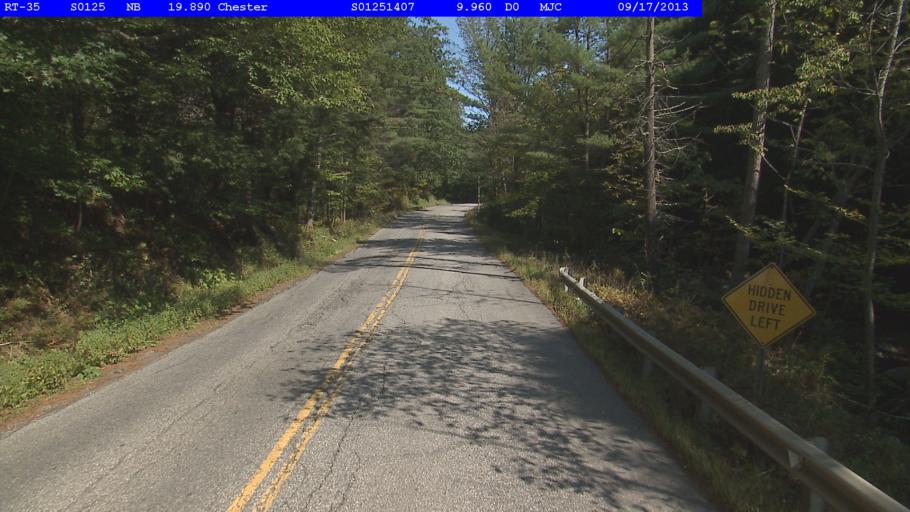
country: US
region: Vermont
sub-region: Windsor County
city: Chester
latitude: 43.2469
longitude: -72.6038
